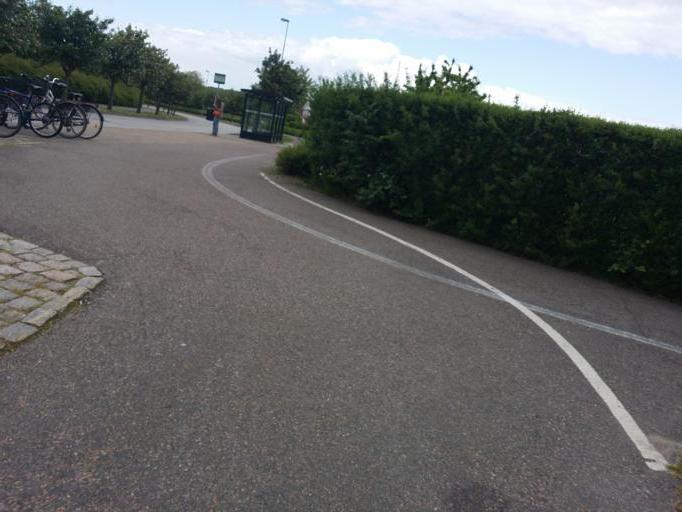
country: SE
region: Skane
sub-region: Burlovs Kommun
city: Arloev
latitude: 55.6001
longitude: 13.0911
